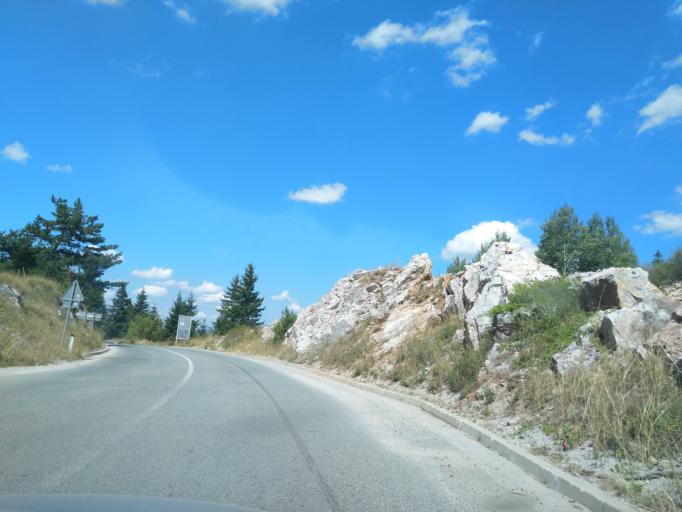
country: RS
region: Central Serbia
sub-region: Zlatiborski Okrug
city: Nova Varos
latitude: 43.4046
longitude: 19.8440
